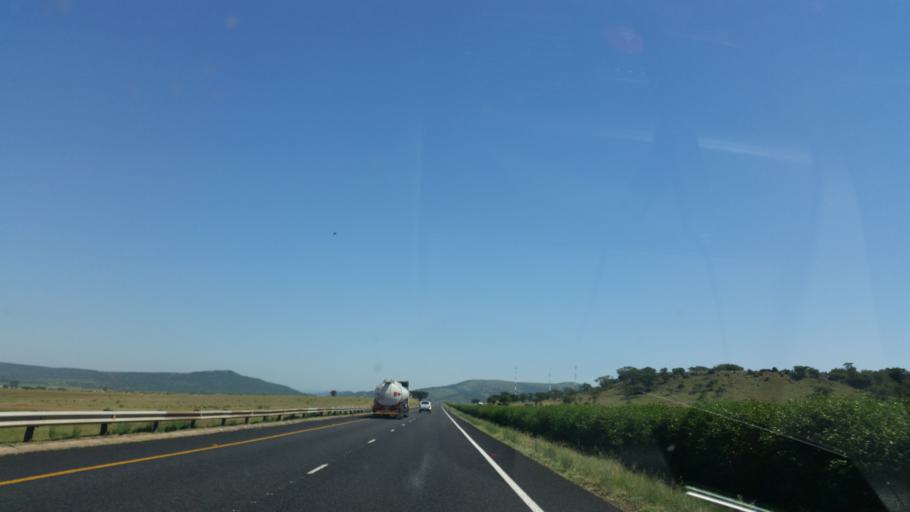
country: ZA
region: KwaZulu-Natal
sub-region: uThukela District Municipality
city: Ladysmith
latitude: -28.7910
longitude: 29.6837
